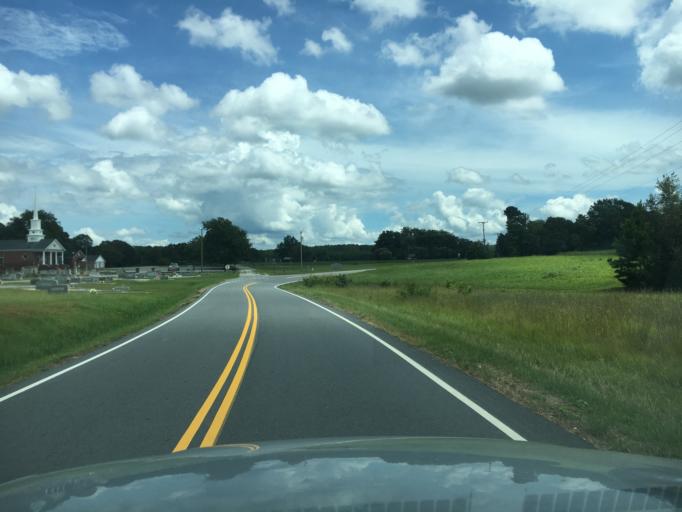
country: US
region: South Carolina
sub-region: Anderson County
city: Belton
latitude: 34.5369
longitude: -82.4384
